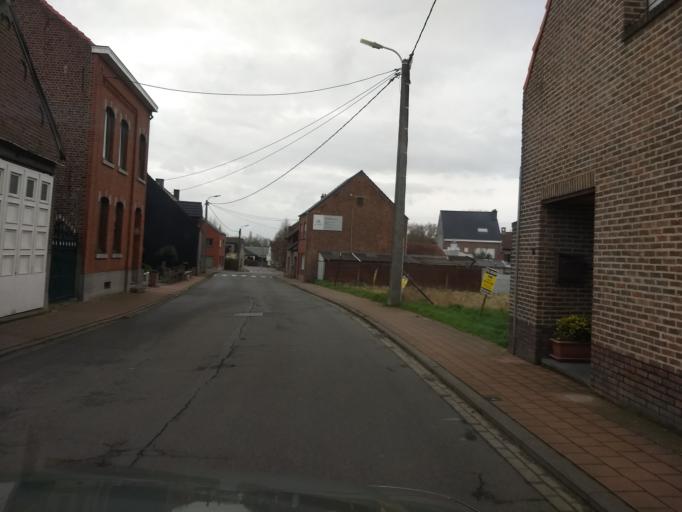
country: BE
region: Flanders
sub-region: Provincie Vlaams-Brabant
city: Liedekerke
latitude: 50.8577
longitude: 4.0697
